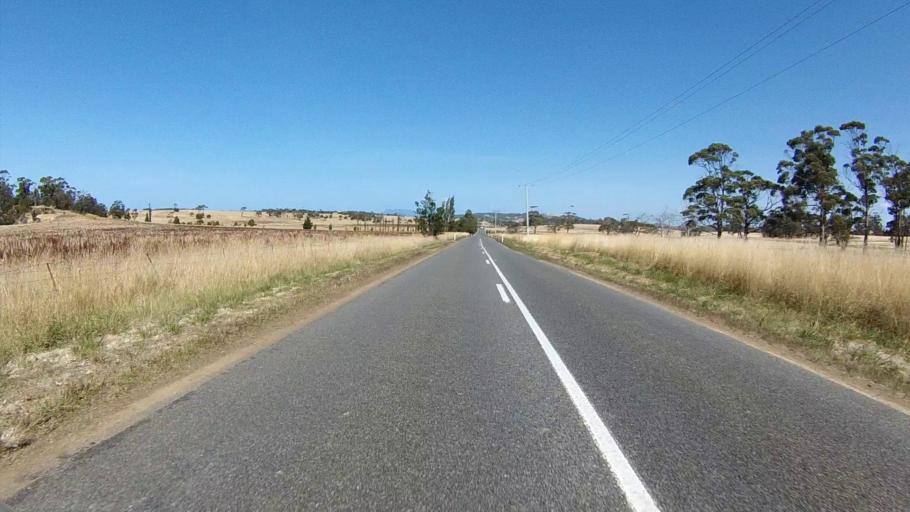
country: AU
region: Tasmania
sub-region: Sorell
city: Sorell
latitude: -42.2686
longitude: 148.0036
